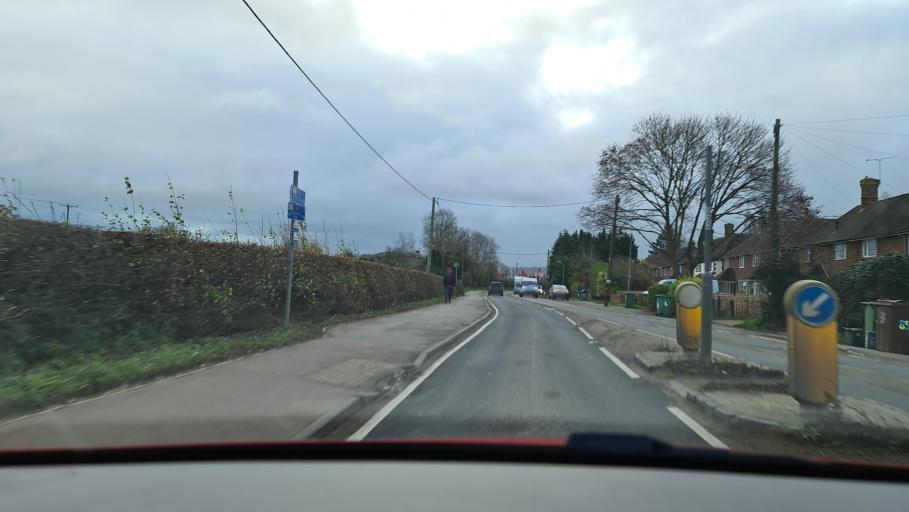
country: GB
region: England
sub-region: Buckinghamshire
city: Aylesbury
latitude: 51.7901
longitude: -0.7984
